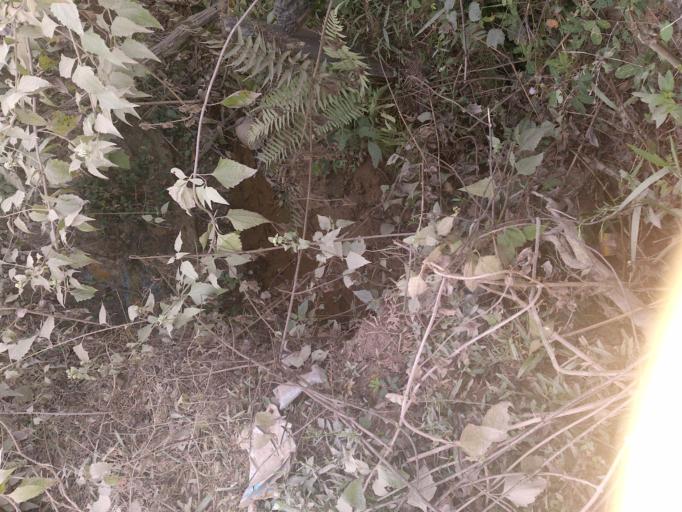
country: LA
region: Xiangkhoang
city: Muang Phonsavan
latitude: 19.3395
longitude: 103.5687
